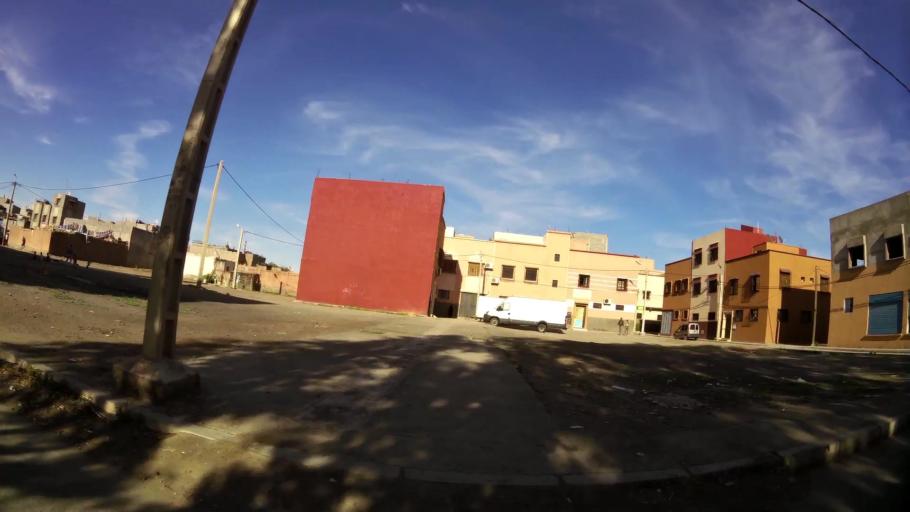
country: MA
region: Marrakech-Tensift-Al Haouz
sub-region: Marrakech
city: Marrakesh
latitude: 31.6862
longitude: -8.0623
